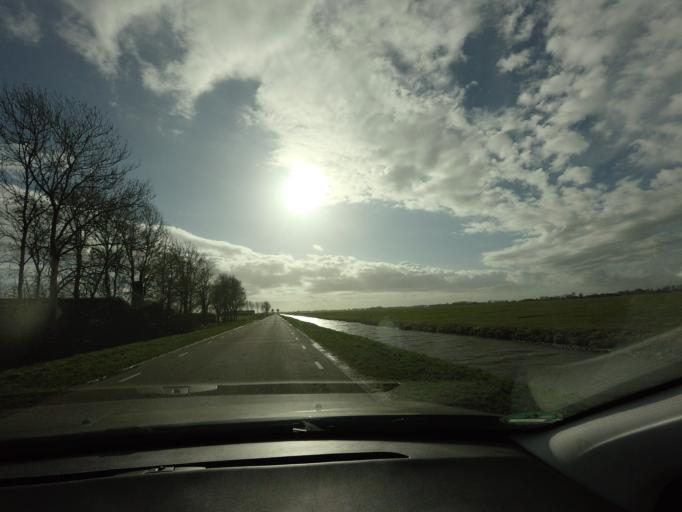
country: NL
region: Friesland
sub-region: Sudwest Fryslan
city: Scharnegoutum
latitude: 53.0552
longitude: 5.7336
